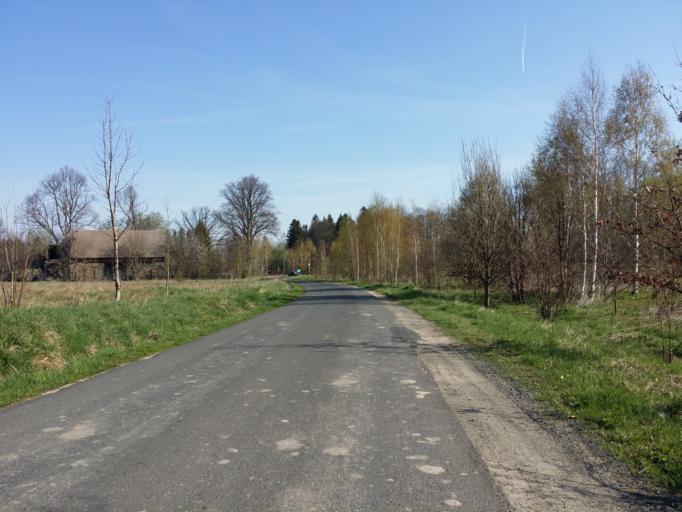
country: PL
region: Lower Silesian Voivodeship
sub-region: Powiat lwowecki
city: Mirsk
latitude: 50.9547
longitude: 15.4294
